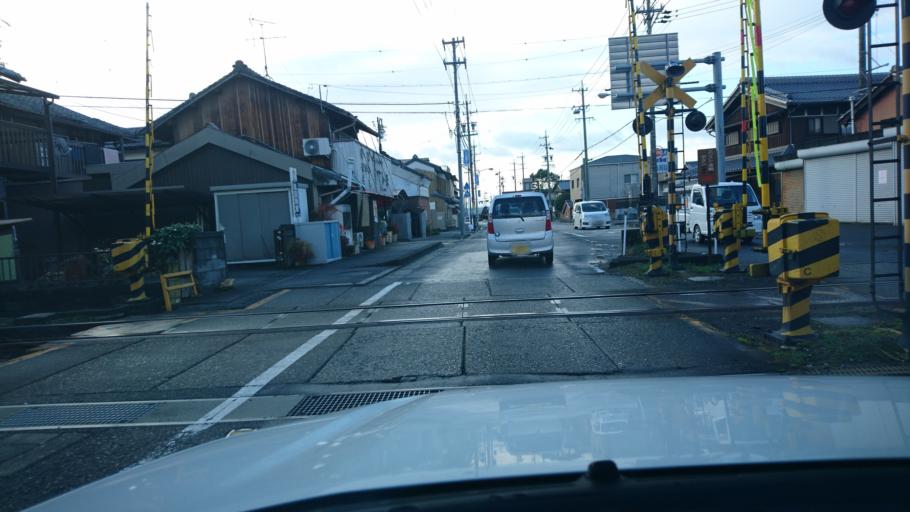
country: JP
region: Mie
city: Ueno-ebisumachi
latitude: 34.7669
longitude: 136.1231
